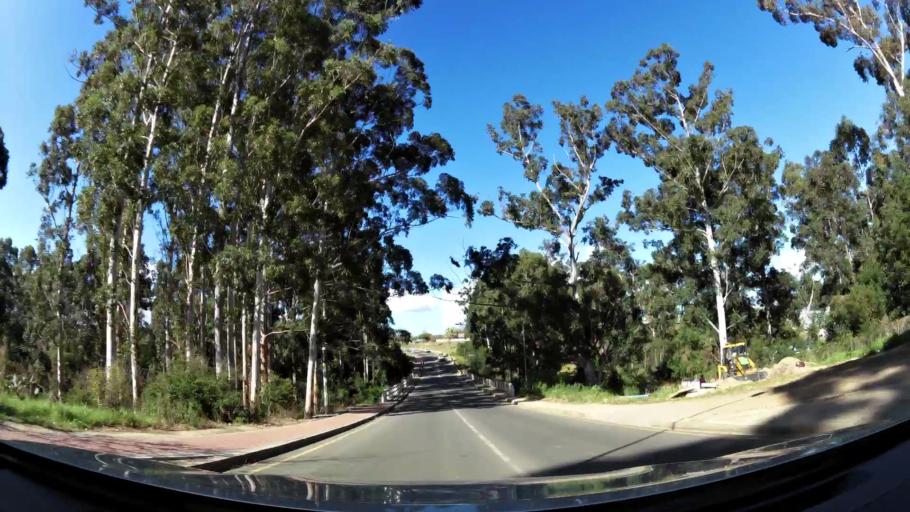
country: ZA
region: Western Cape
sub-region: Eden District Municipality
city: George
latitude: -33.9501
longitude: 22.4231
